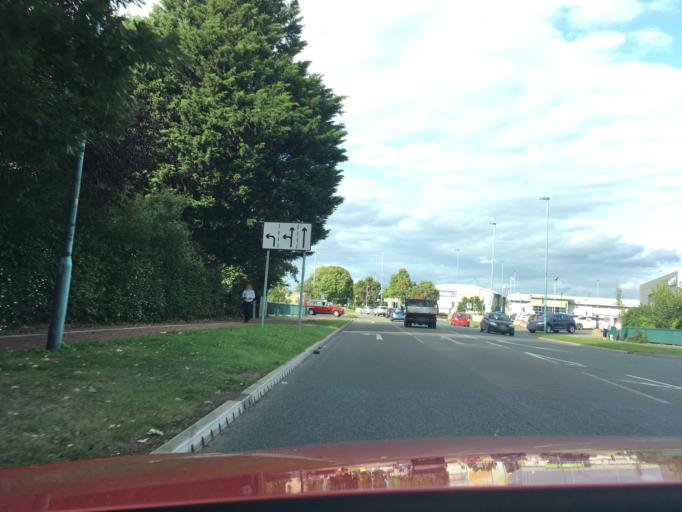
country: GB
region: England
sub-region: Gloucestershire
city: Swindon
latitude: 51.9126
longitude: -2.1006
